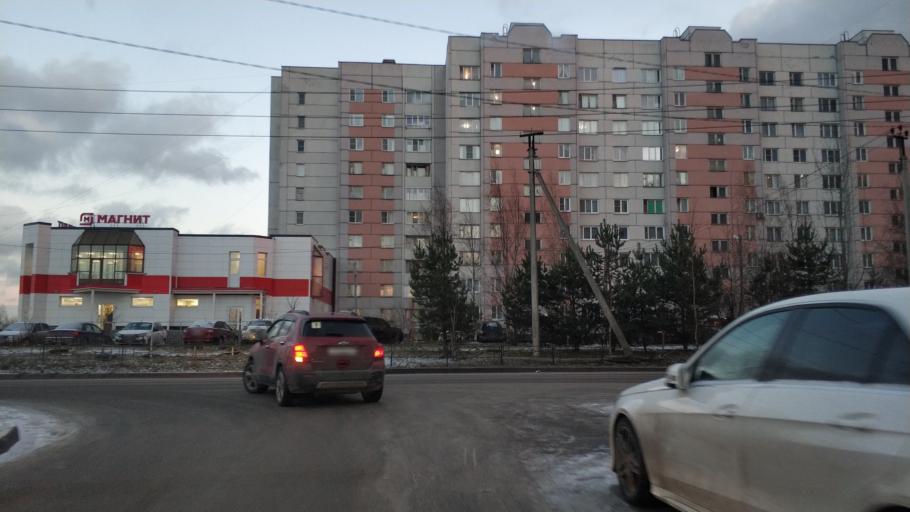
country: RU
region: St.-Petersburg
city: Pontonnyy
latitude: 59.8002
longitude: 30.6374
